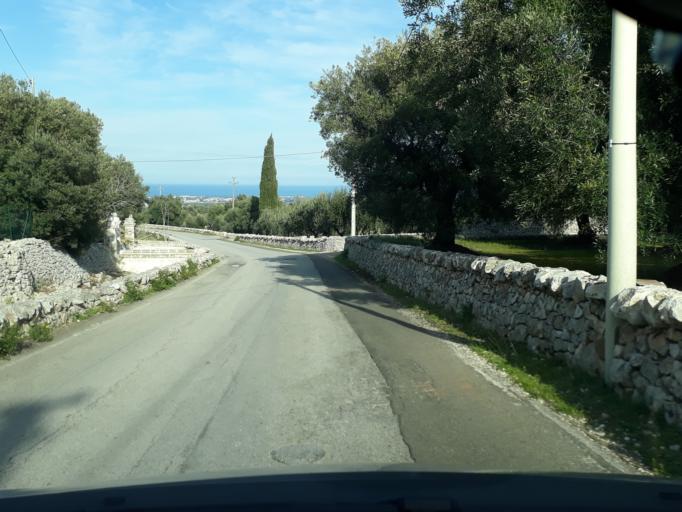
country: IT
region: Apulia
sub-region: Provincia di Brindisi
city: Lamie di Olimpie-Selva
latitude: 40.8086
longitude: 17.3543
